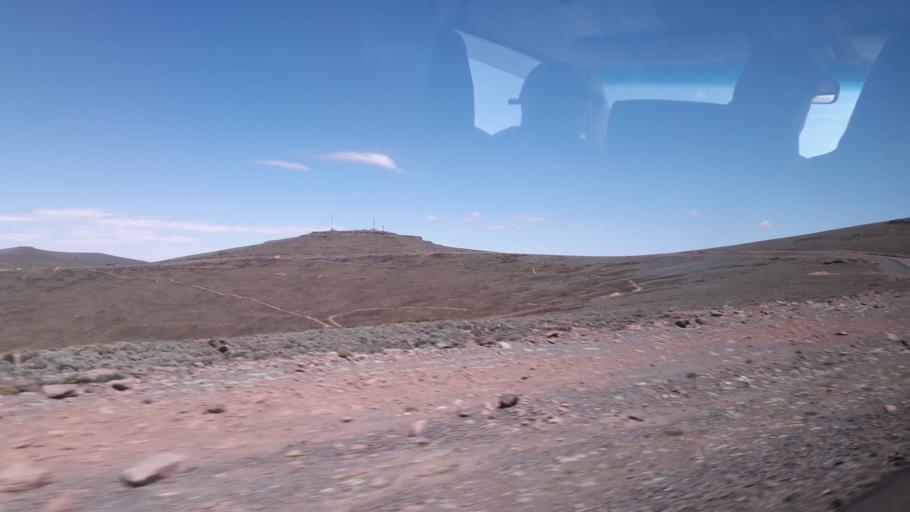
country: ZA
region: Orange Free State
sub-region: Thabo Mofutsanyana District Municipality
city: Phuthaditjhaba
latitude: -28.8140
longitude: 28.7356
